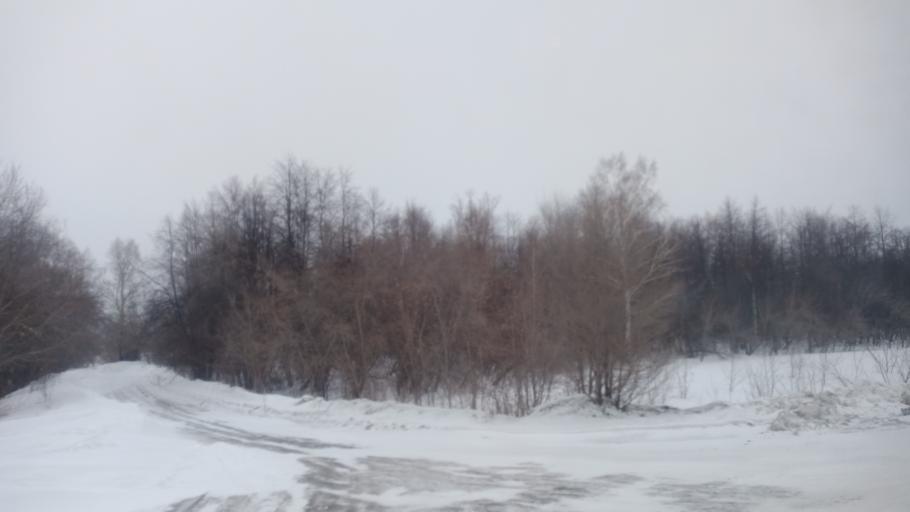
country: RU
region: Altai Krai
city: Nauchnyy Gorodok
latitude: 53.4205
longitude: 83.5314
